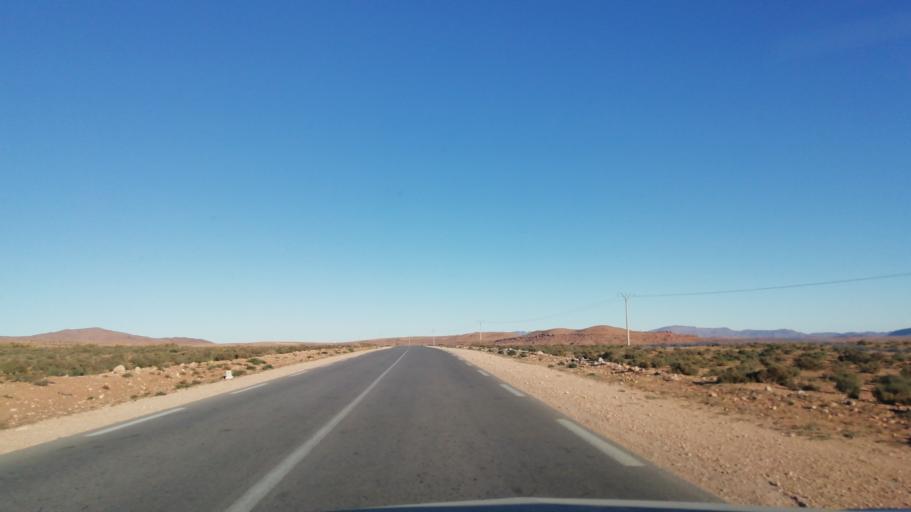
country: DZ
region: El Bayadh
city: El Abiodh Sidi Cheikh
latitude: 33.1615
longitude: 0.3996
